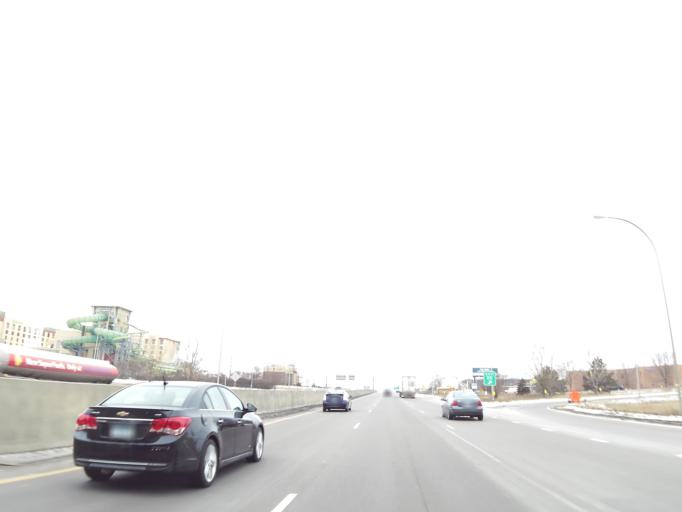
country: US
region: Minnesota
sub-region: Hennepin County
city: Richfield
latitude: 44.8623
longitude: -93.2477
